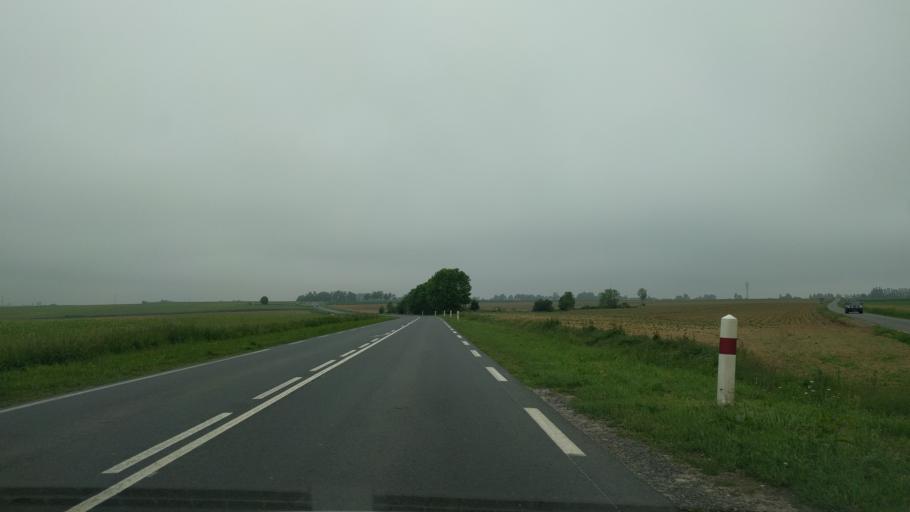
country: FR
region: Picardie
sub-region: Departement de la Somme
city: Moislains
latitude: 50.0140
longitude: 2.9120
